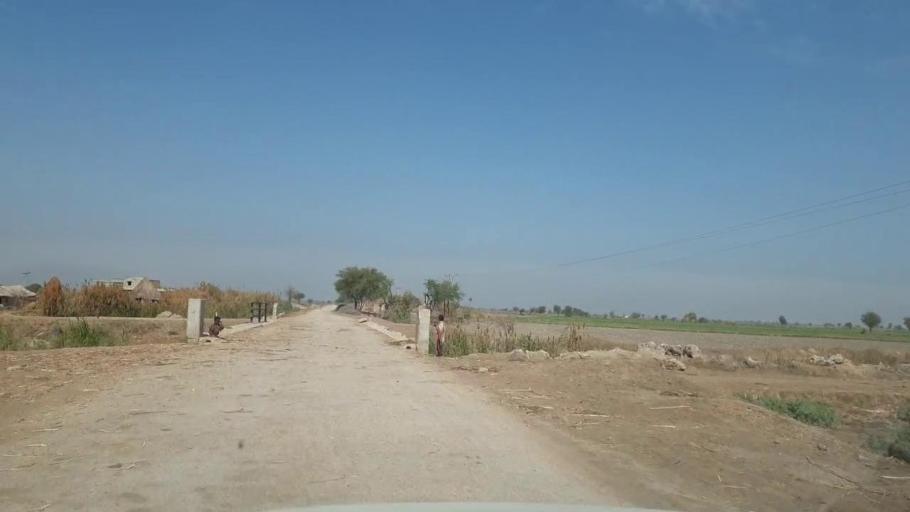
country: PK
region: Sindh
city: Pithoro
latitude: 25.5612
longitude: 69.2089
